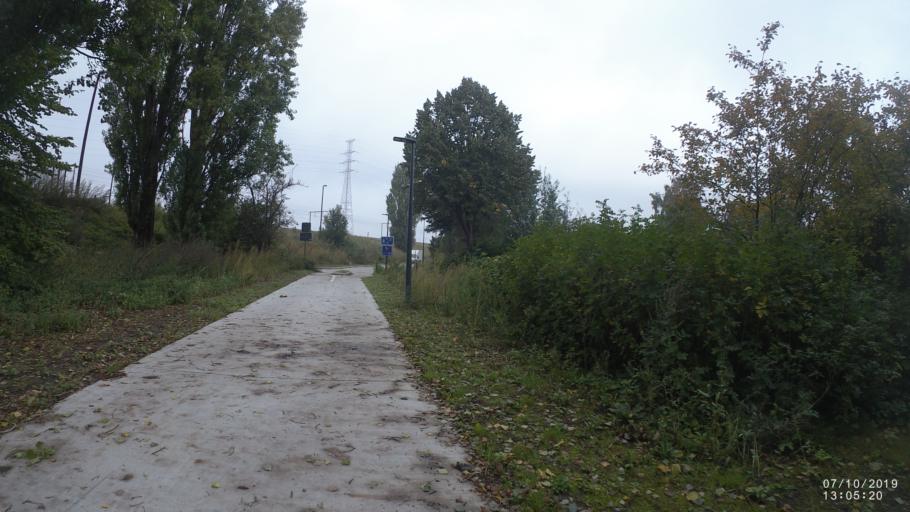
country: BE
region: Flanders
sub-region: Provincie Oost-Vlaanderen
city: Ledeberg
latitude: 51.0723
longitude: 3.7454
